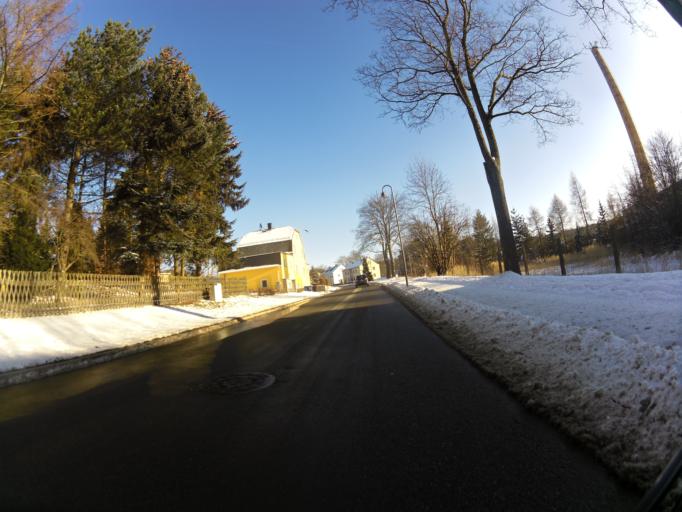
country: DE
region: Thuringia
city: Tanna
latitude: 50.4899
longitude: 11.8753
